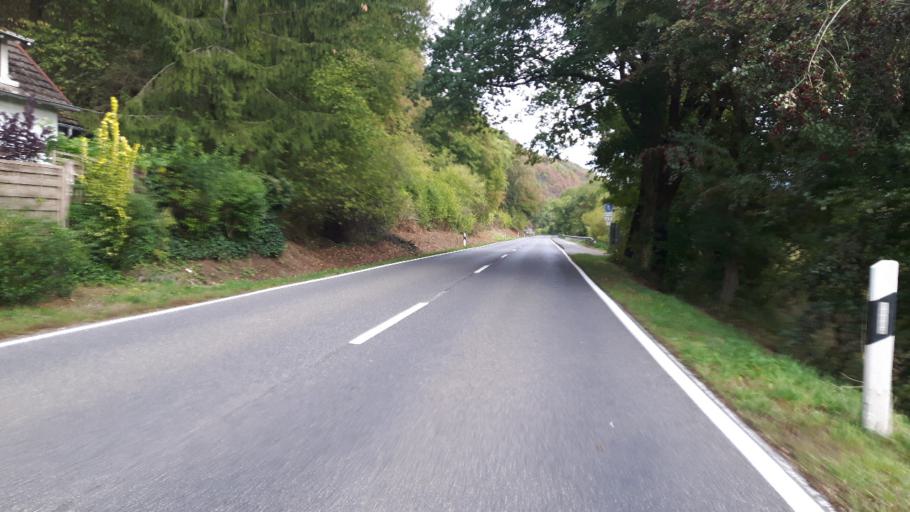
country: DE
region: North Rhine-Westphalia
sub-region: Regierungsbezirk Koln
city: Eitorf
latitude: 50.7694
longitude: 7.4939
